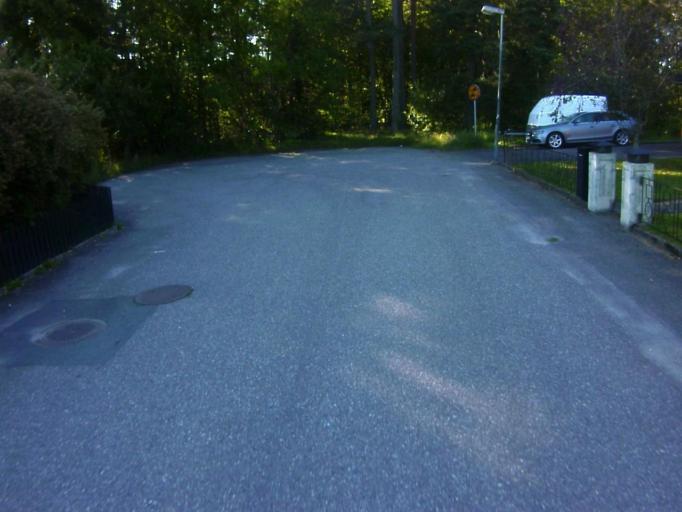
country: SE
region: Soedermanland
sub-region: Eskilstuna Kommun
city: Skogstorp
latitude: 59.3335
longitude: 16.4376
